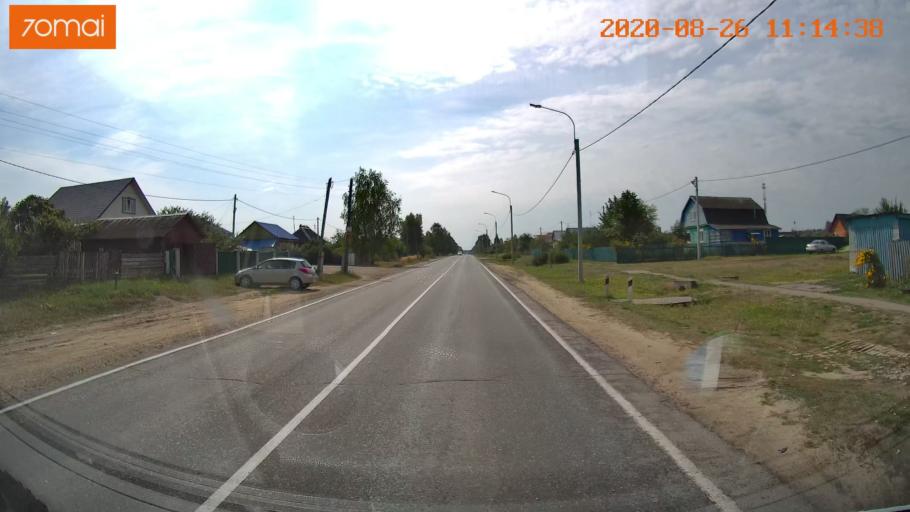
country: RU
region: Rjazan
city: Izhevskoye
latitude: 54.4471
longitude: 41.1164
